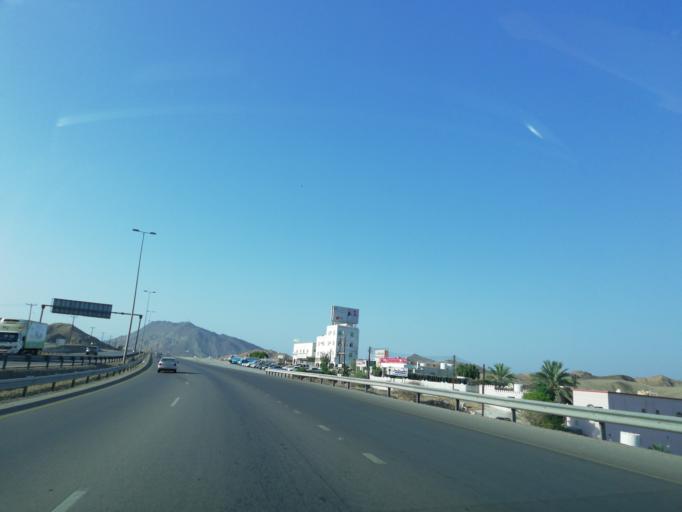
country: OM
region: Muhafazat ad Dakhiliyah
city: Bidbid
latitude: 23.4297
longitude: 58.1201
